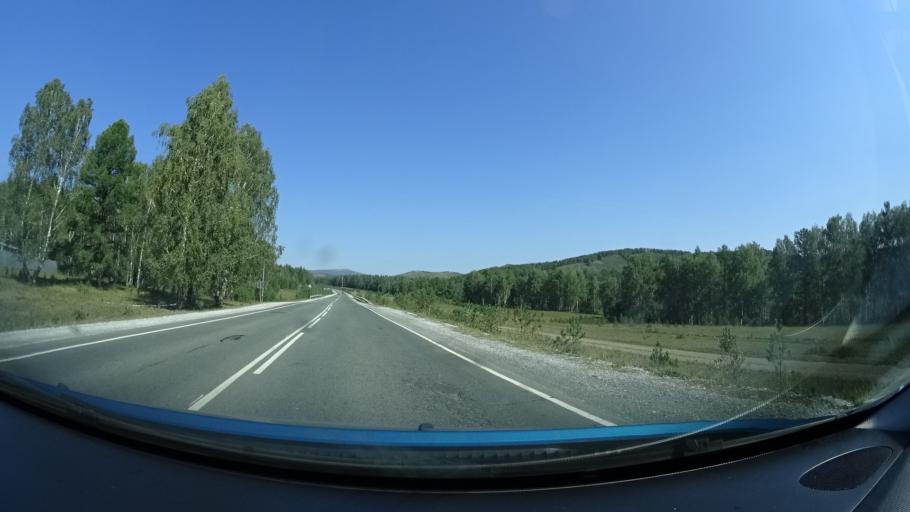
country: RU
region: Bashkortostan
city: Abzakovo
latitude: 53.8457
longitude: 58.5826
